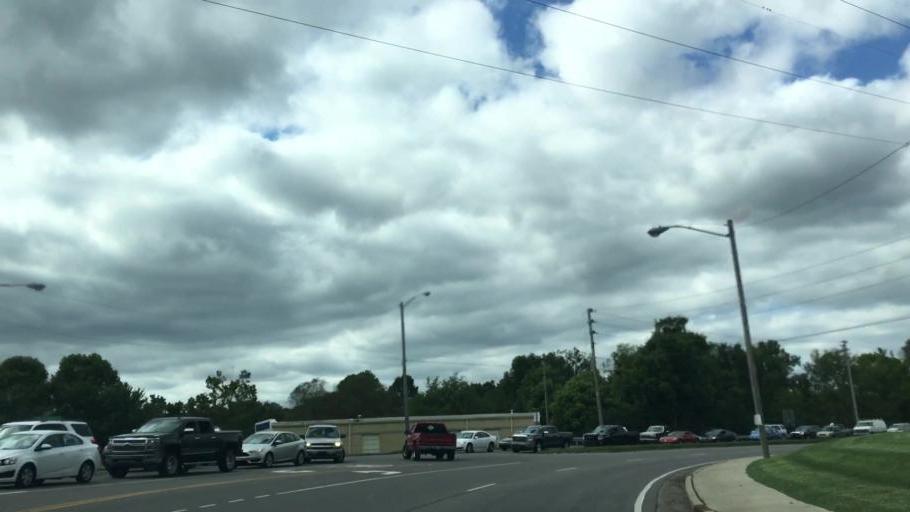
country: US
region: Tennessee
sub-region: Maury County
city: Columbia
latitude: 35.6054
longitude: -87.0672
